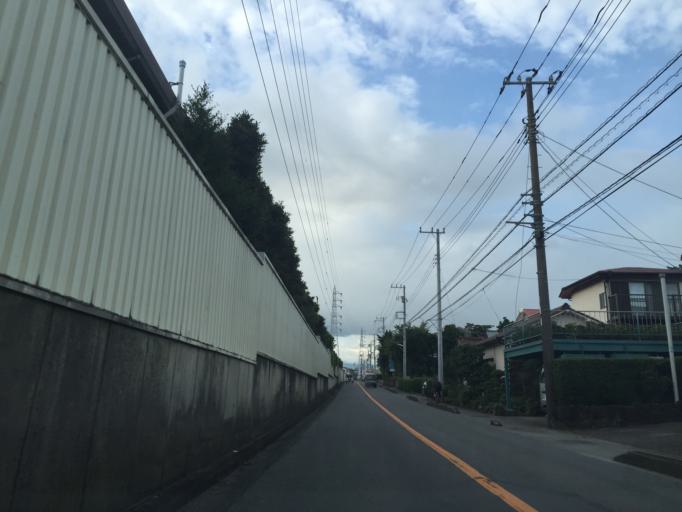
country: JP
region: Shizuoka
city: Mishima
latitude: 35.1602
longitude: 138.9104
